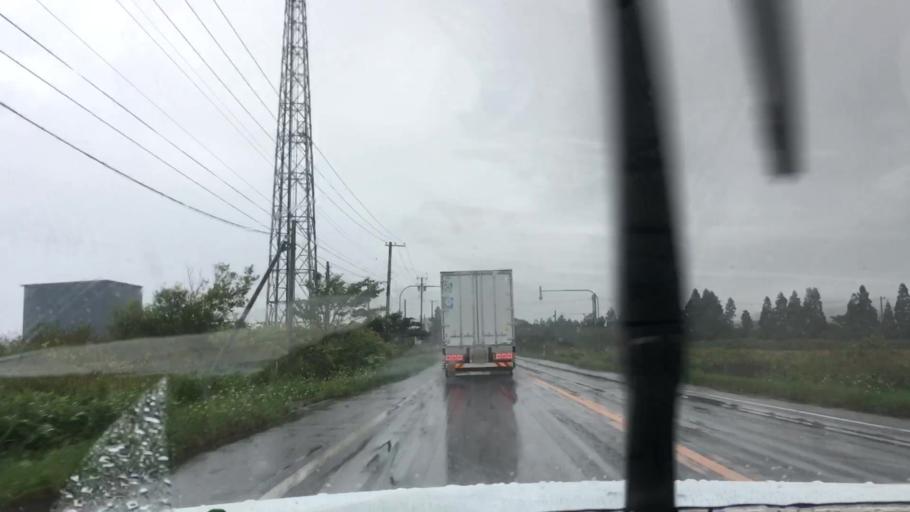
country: JP
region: Hokkaido
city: Niseko Town
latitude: 42.4730
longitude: 140.3451
